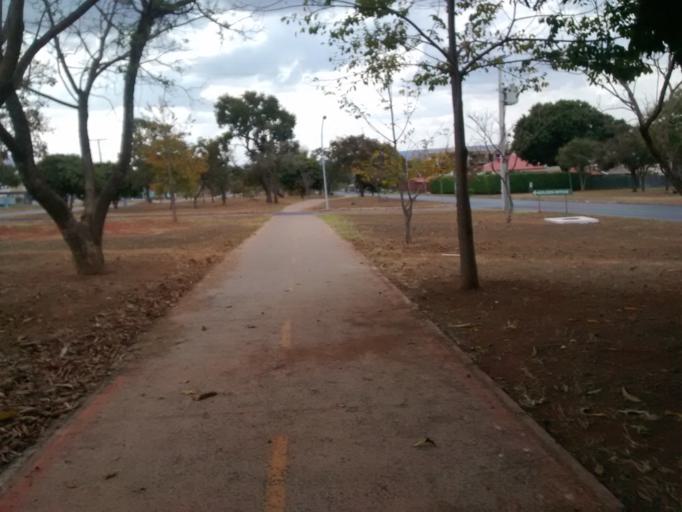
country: BR
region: Federal District
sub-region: Brasilia
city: Brasilia
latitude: -15.7427
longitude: -47.9010
